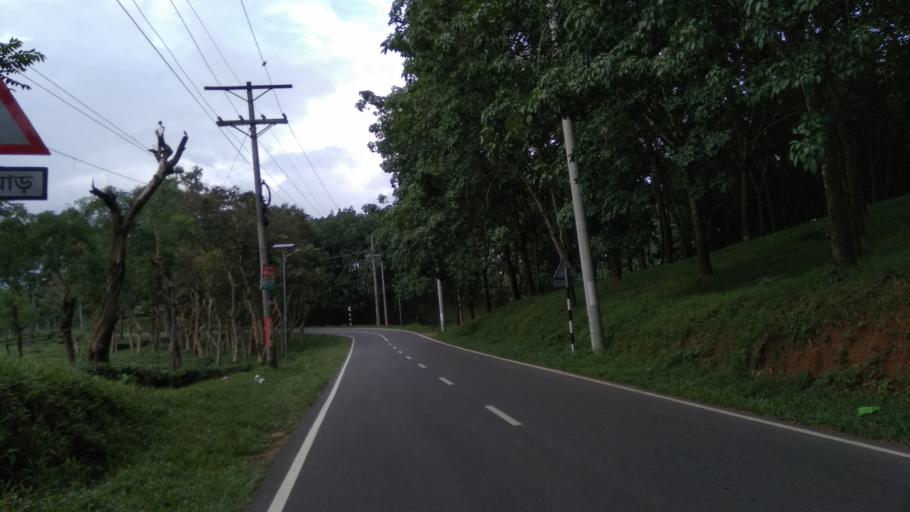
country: IN
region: Tripura
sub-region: Dhalai
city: Kamalpur
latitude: 24.3011
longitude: 91.7542
